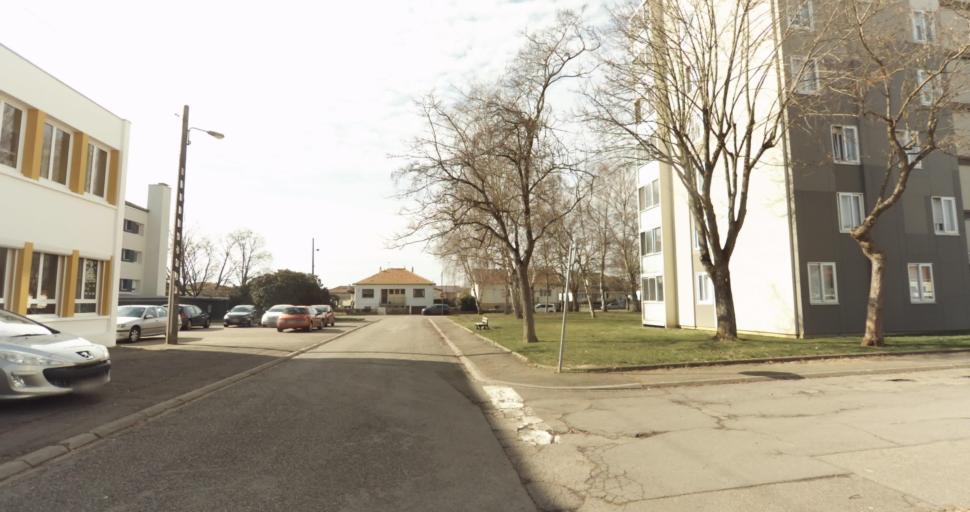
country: FR
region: Lorraine
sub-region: Departement de Meurthe-et-Moselle
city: Jarny
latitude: 49.1550
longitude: 5.8757
